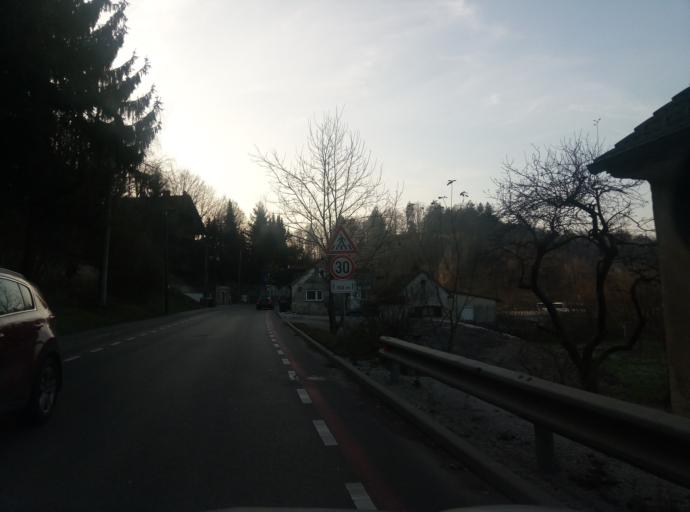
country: SI
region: Ljubljana
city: Ljubljana
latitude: 46.0440
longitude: 14.5193
